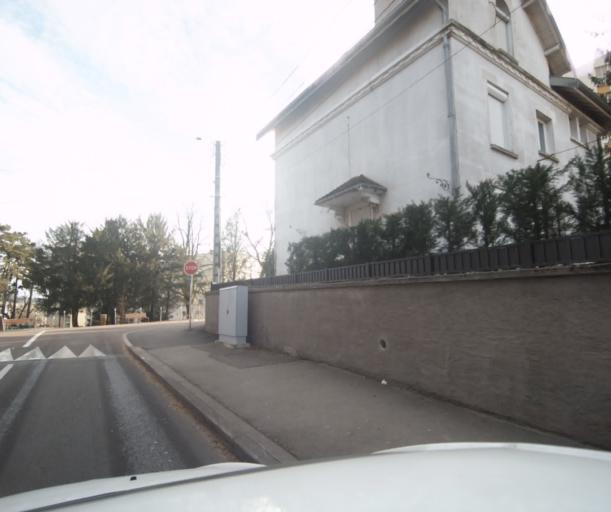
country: FR
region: Franche-Comte
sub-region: Departement du Doubs
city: Besancon
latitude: 47.2585
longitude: 6.0208
